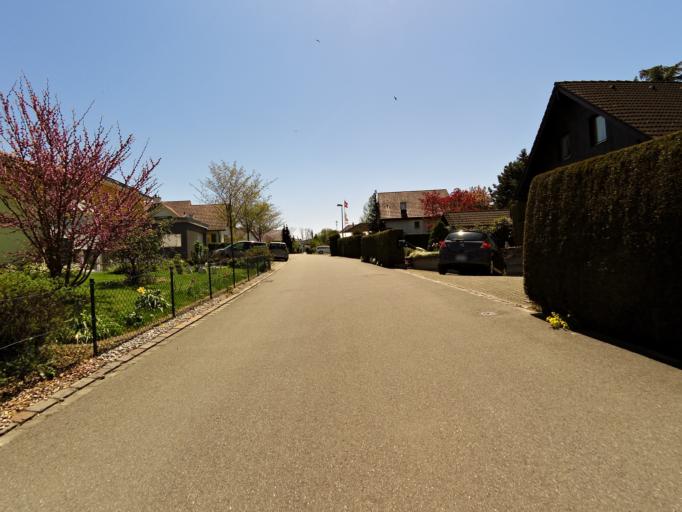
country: CH
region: Thurgau
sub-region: Weinfelden District
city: Berg
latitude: 47.6093
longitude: 9.1690
